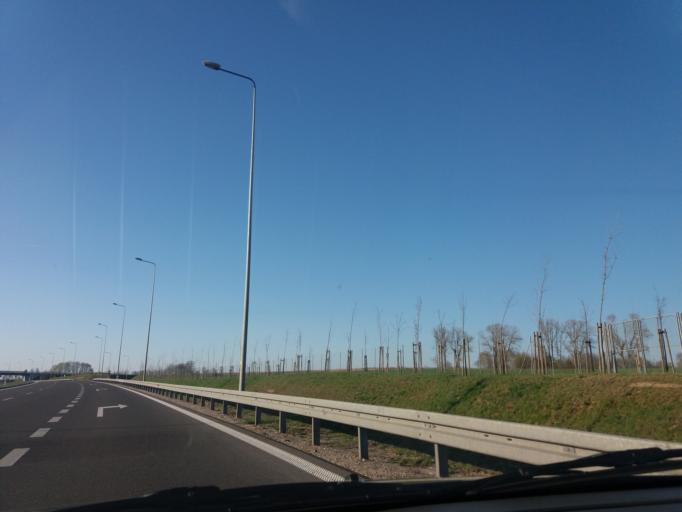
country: PL
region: Warmian-Masurian Voivodeship
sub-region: Powiat nidzicki
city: Nidzica
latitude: 53.3296
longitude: 20.4393
